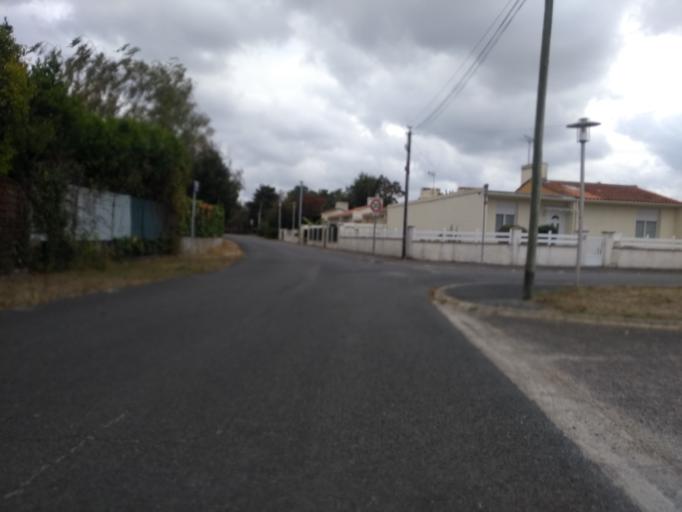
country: FR
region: Aquitaine
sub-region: Departement de la Gironde
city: Pessac
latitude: 44.8030
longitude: -0.6567
